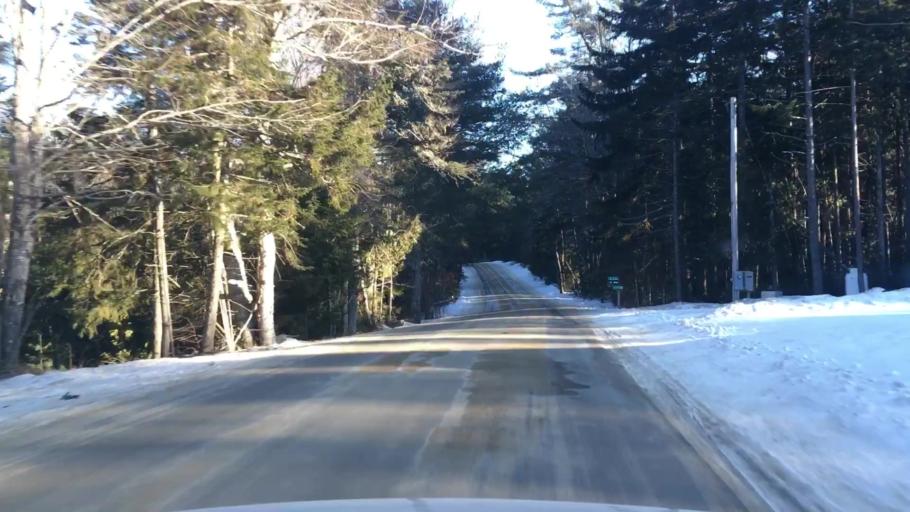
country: US
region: Maine
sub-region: Hancock County
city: Castine
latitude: 44.3835
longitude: -68.7338
